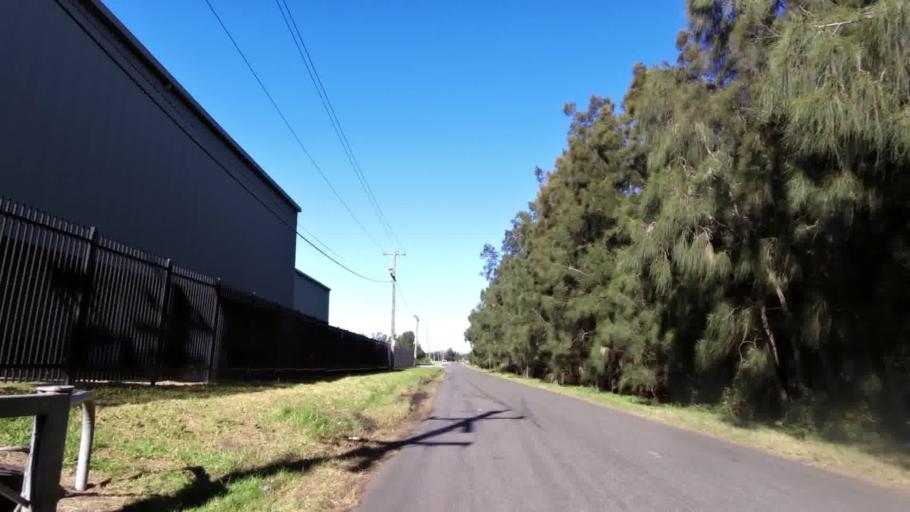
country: AU
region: New South Wales
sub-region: Wollongong
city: Berkeley
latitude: -34.4782
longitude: 150.8339
